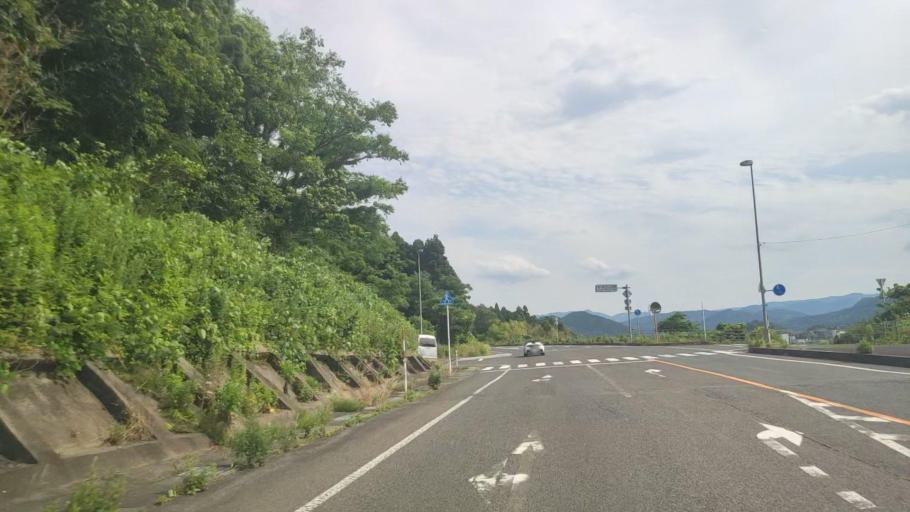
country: JP
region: Tottori
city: Tottori
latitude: 35.4125
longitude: 134.2064
